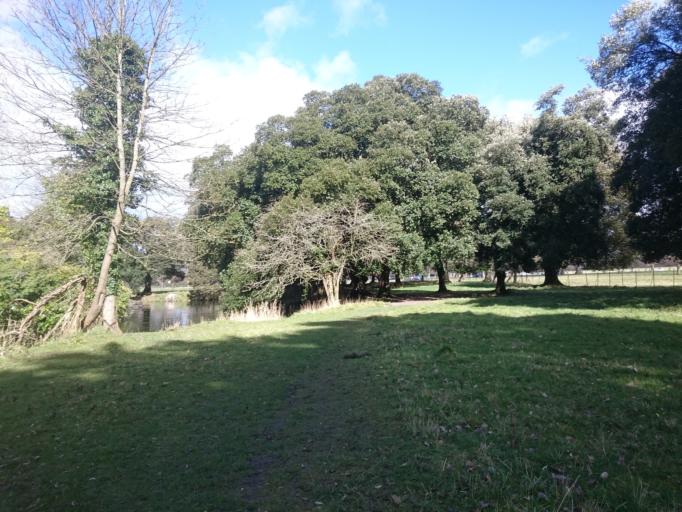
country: IE
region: Leinster
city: Chapelizod
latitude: 53.3647
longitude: -6.3418
